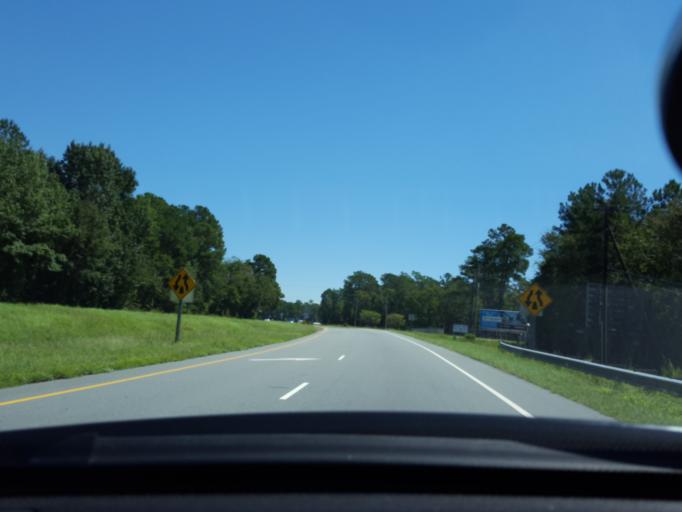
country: US
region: North Carolina
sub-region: Bladen County
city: Elizabethtown
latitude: 34.6470
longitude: -78.5552
